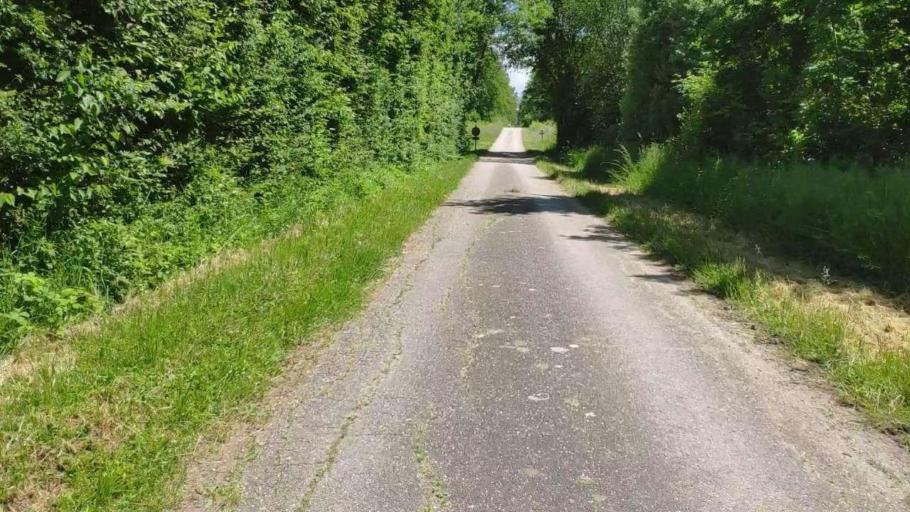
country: FR
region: Franche-Comte
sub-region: Departement du Jura
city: Bletterans
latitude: 46.7828
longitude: 5.4554
